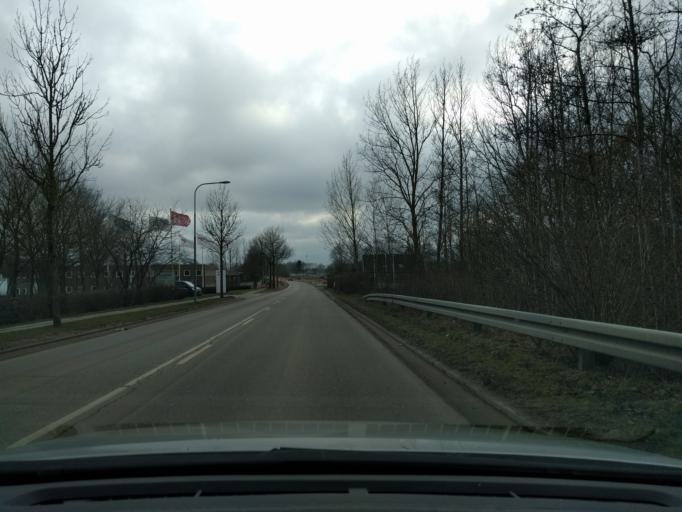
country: DK
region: South Denmark
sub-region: Odense Kommune
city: Bellinge
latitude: 55.3635
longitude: 10.3262
